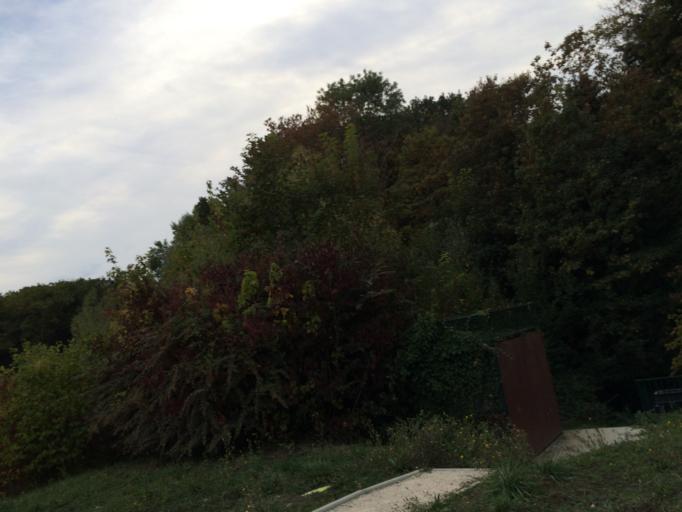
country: FR
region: Ile-de-France
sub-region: Departement de l'Essonne
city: Linas
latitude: 48.6371
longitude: 2.2557
